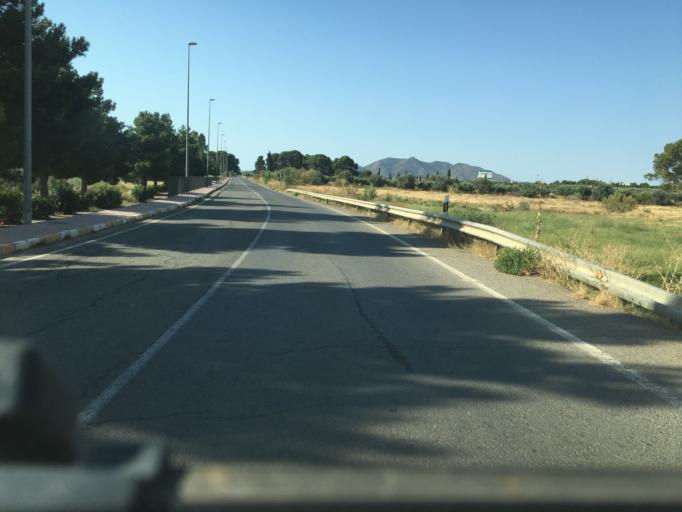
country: ES
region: Murcia
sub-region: Murcia
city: Puerto Lumbreras
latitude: 37.5488
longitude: -1.8154
